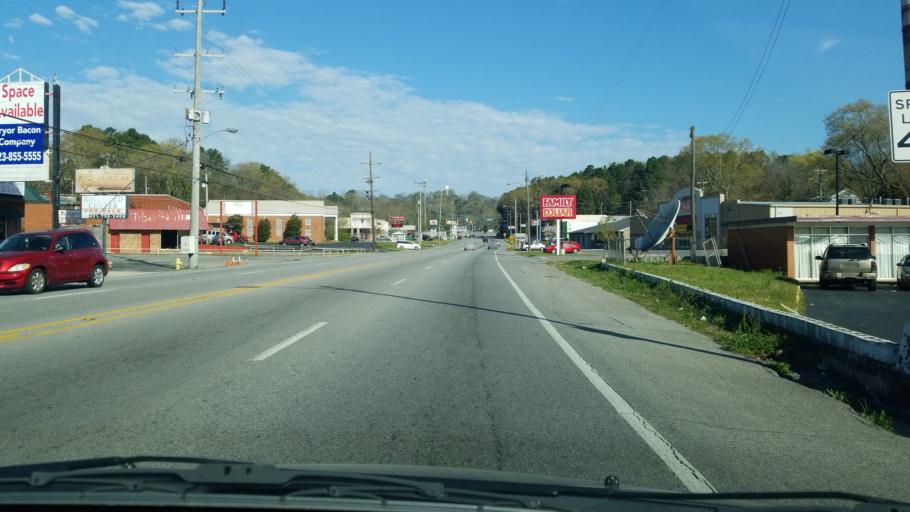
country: US
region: Tennessee
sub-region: Hamilton County
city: East Ridge
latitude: 35.0018
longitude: -85.2587
